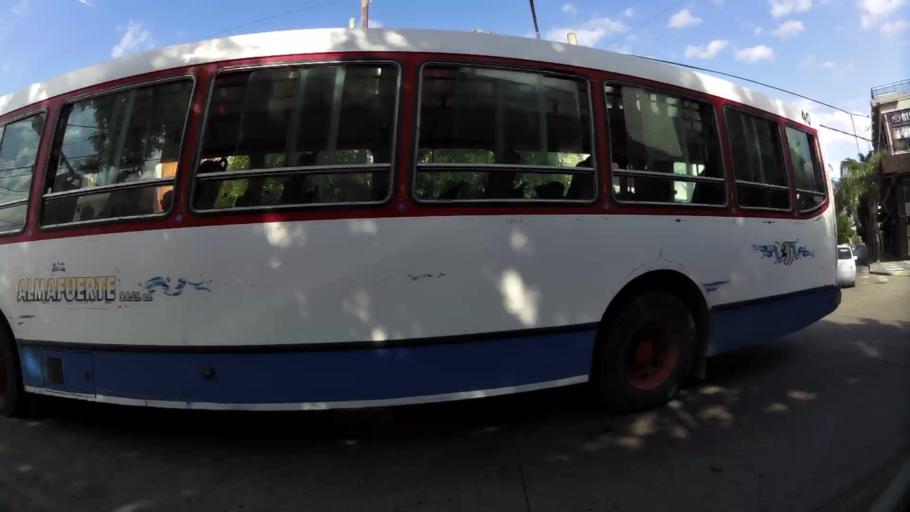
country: AR
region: Buenos Aires
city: San Justo
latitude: -34.6492
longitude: -58.5639
